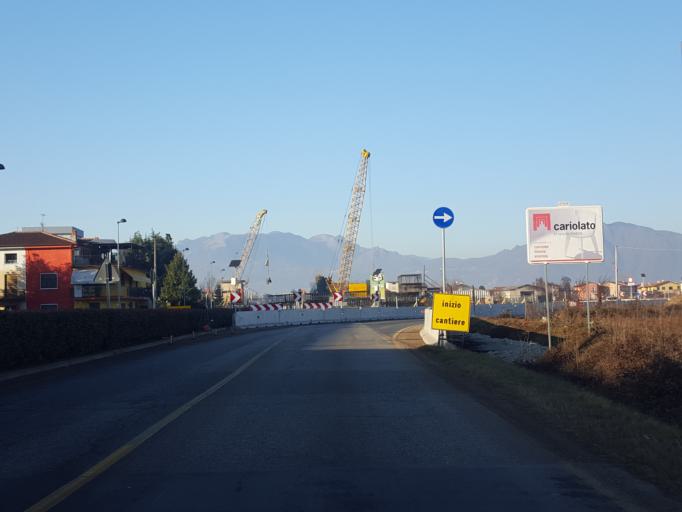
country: IT
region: Veneto
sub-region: Provincia di Vicenza
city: Malo
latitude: 45.6442
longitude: 11.4271
